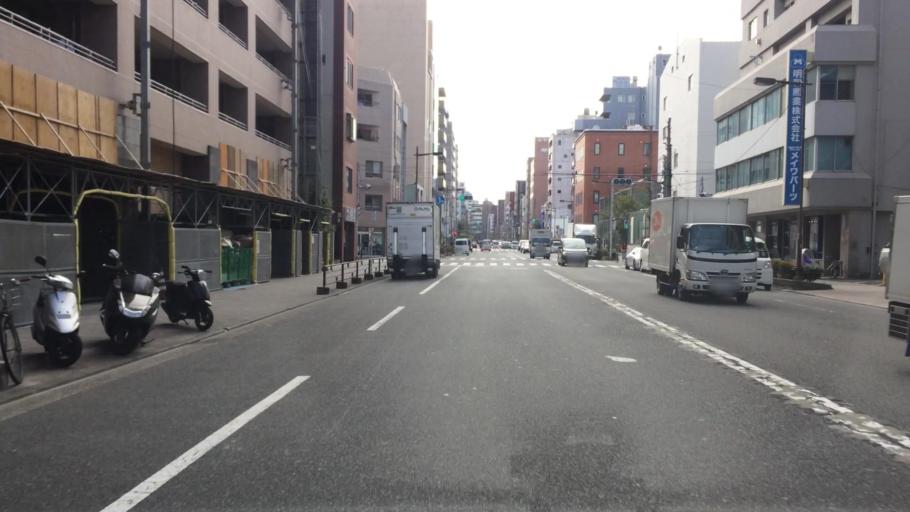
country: JP
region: Tokyo
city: Tokyo
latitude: 35.7080
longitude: 139.7881
